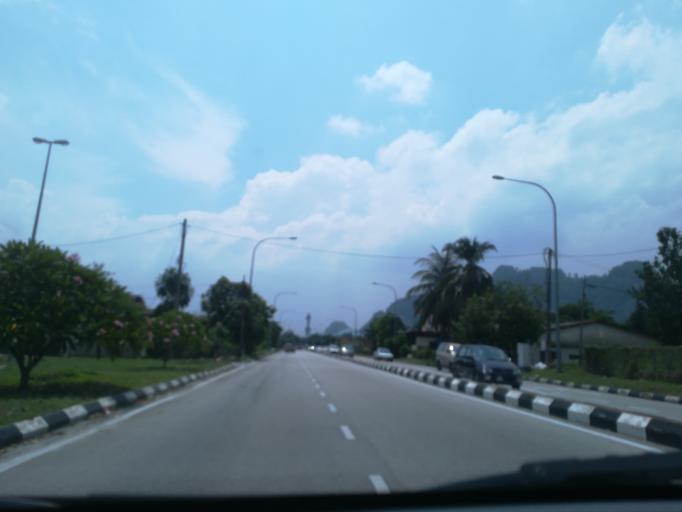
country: MY
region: Perak
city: Ipoh
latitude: 4.5847
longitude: 101.1273
